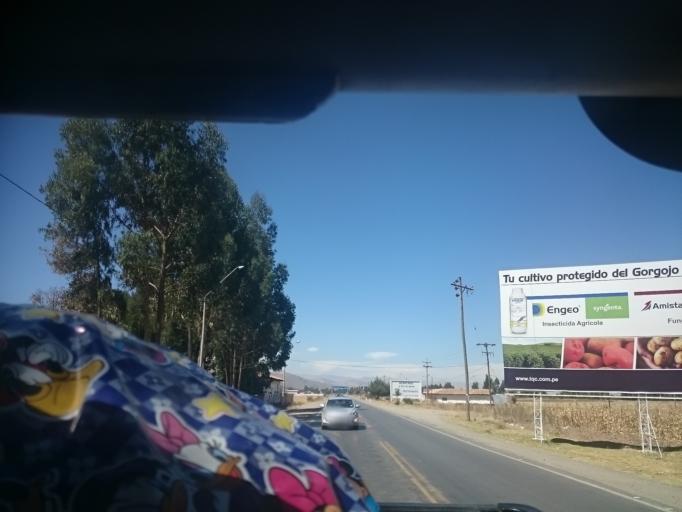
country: PE
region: Junin
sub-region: Provincia de Jauja
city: Sausa
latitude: -11.7872
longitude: -75.4747
